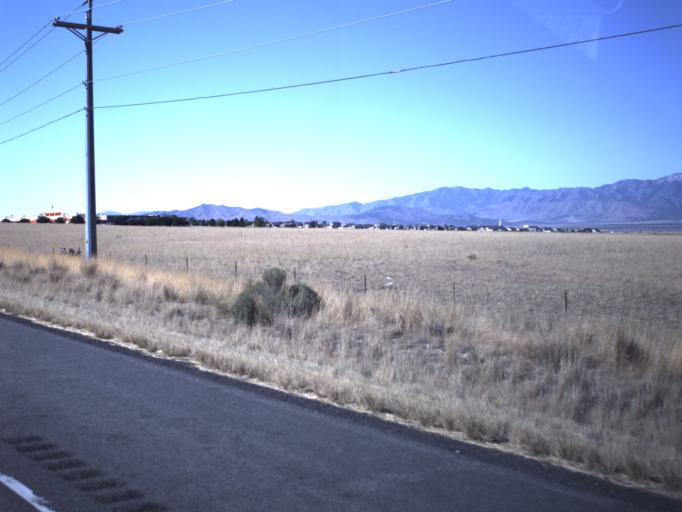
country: US
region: Utah
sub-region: Tooele County
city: Erda
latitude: 40.5771
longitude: -112.2944
